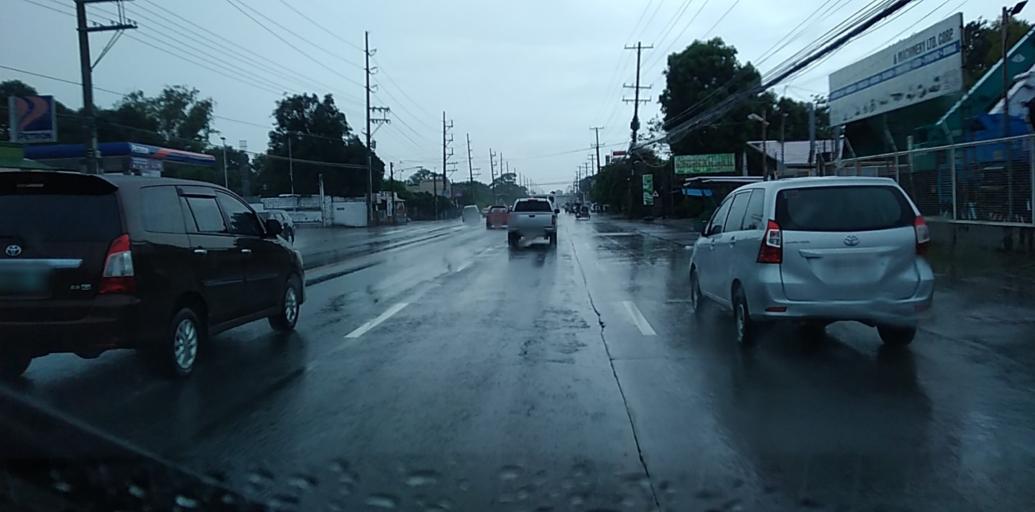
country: PH
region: Central Luzon
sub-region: Province of Pampanga
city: Bulaon
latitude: 15.0606
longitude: 120.6556
